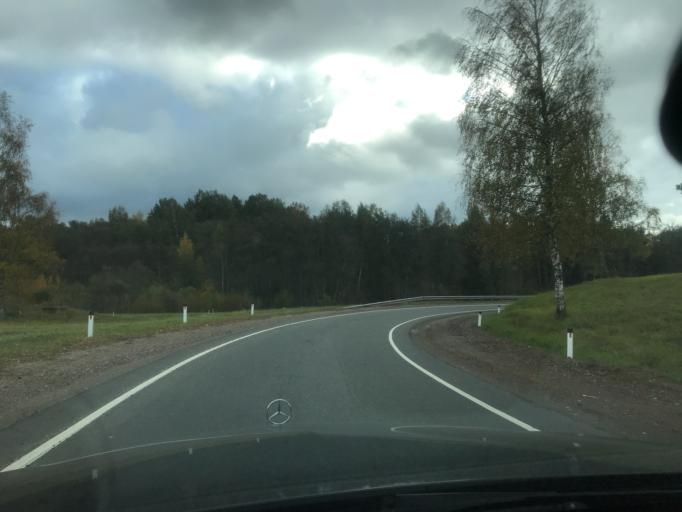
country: RU
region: Pskov
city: Pustoshka
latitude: 56.3139
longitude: 29.3927
